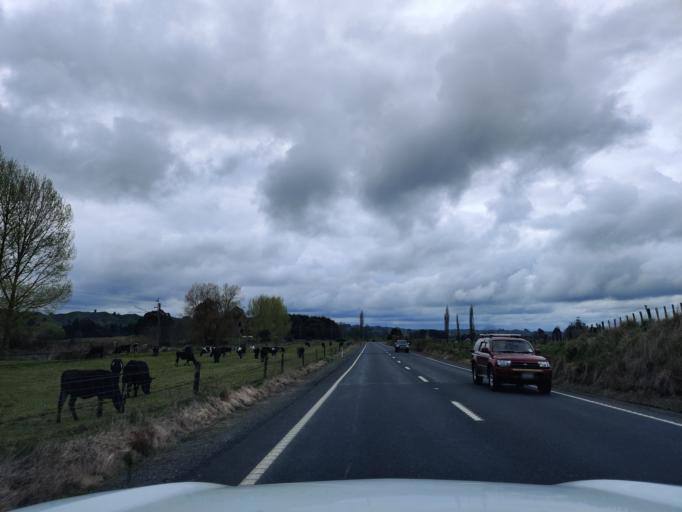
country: NZ
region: Waikato
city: Turangi
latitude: -39.0254
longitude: 175.3816
